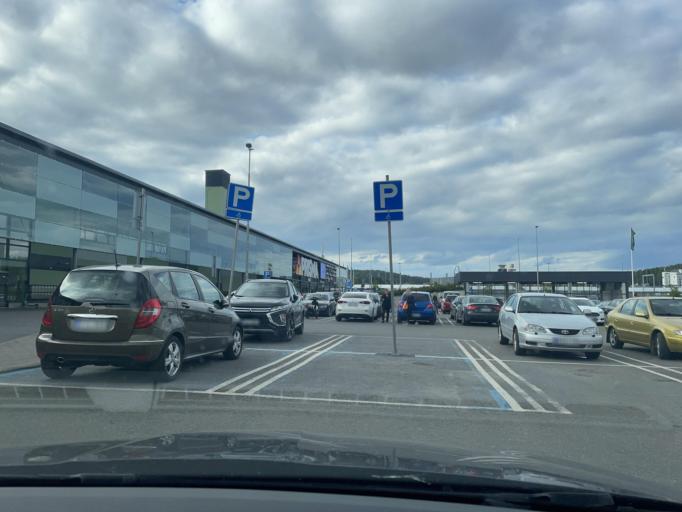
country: FI
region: Central Finland
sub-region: Jyvaeskylae
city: Jyvaeskylae
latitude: 62.2569
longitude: 25.7747
